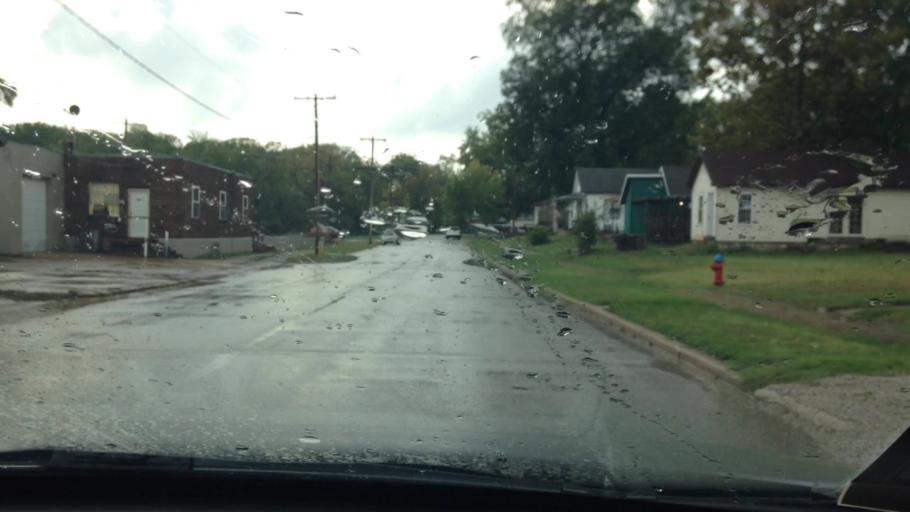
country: US
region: Kansas
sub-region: Leavenworth County
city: Leavenworth
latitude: 39.3196
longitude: -94.9268
